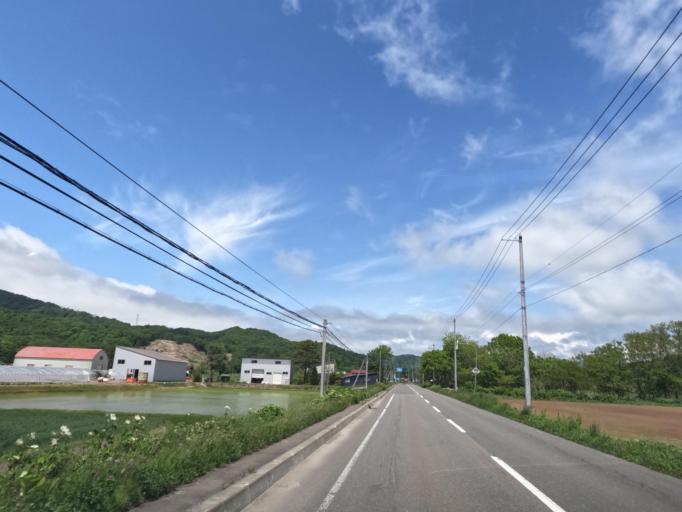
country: JP
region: Hokkaido
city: Tobetsu
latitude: 43.2900
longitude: 141.5383
